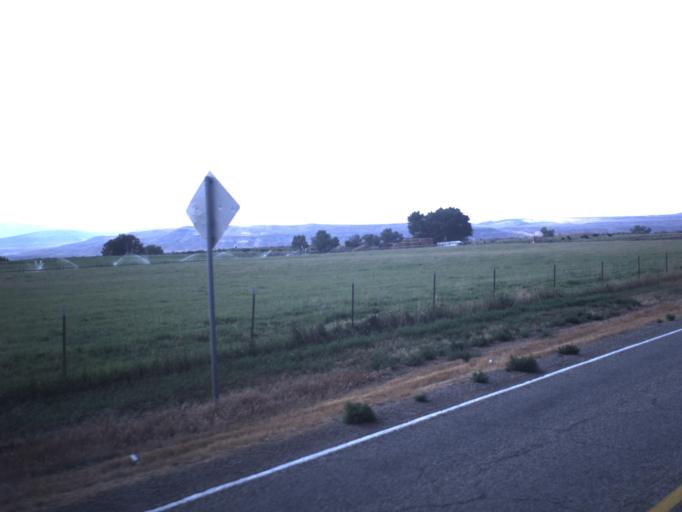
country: US
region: Utah
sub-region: Uintah County
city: Naples
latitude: 40.3979
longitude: -109.3461
